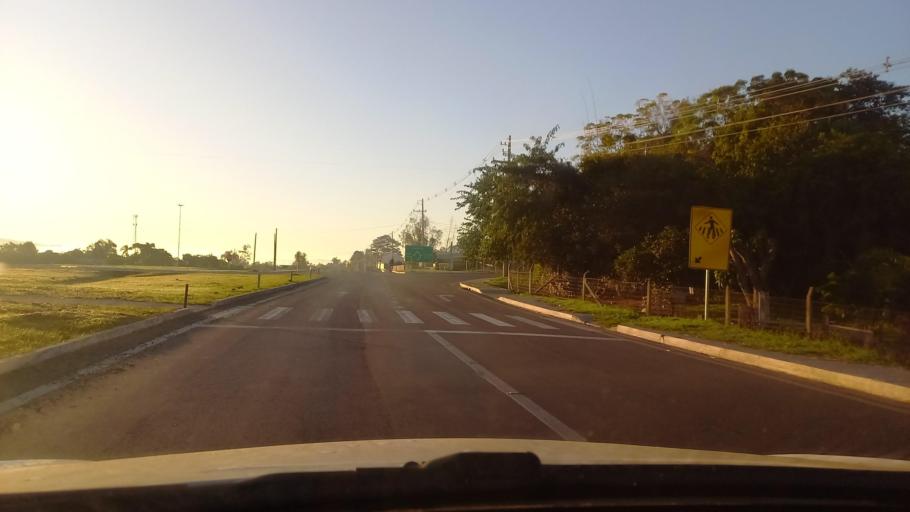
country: BR
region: Rio Grande do Sul
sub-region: Candelaria
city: Candelaria
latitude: -29.6812
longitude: -52.7912
